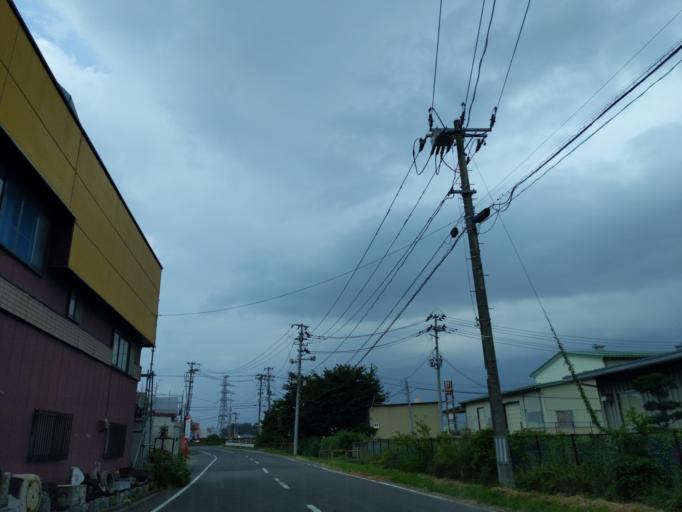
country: JP
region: Fukushima
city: Koriyama
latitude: 37.4480
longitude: 140.3776
